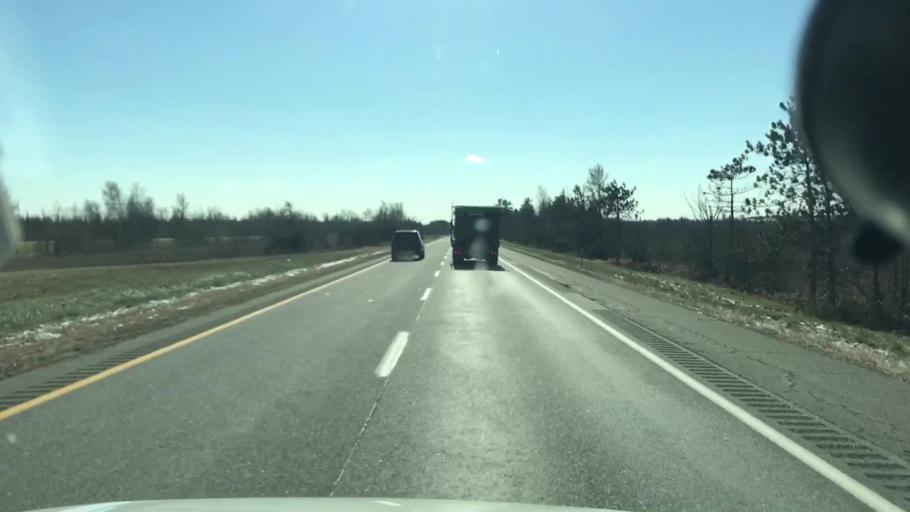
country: US
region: Maine
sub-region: Penobscot County
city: Greenbush
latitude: 45.0114
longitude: -68.7003
